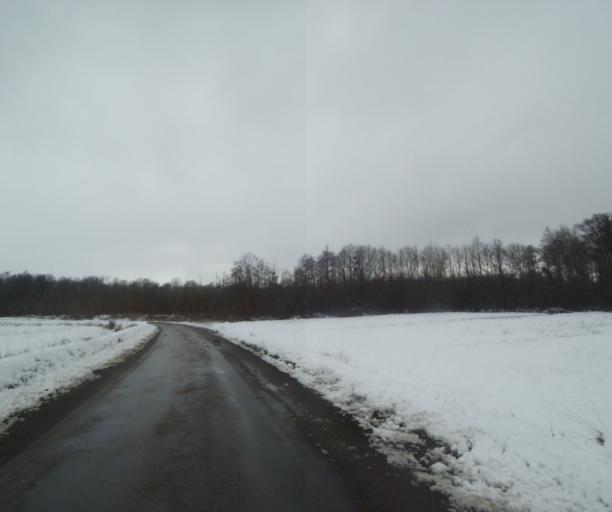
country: FR
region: Champagne-Ardenne
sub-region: Departement de la Haute-Marne
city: Laneuville-a-Remy
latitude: 48.4639
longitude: 4.8288
